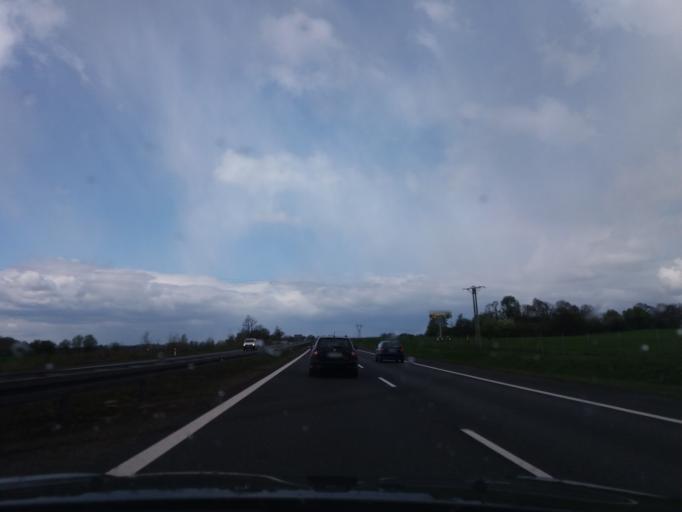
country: PL
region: Silesian Voivodeship
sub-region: Powiat gliwicki
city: Rudziniec
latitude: 50.3985
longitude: 18.4332
